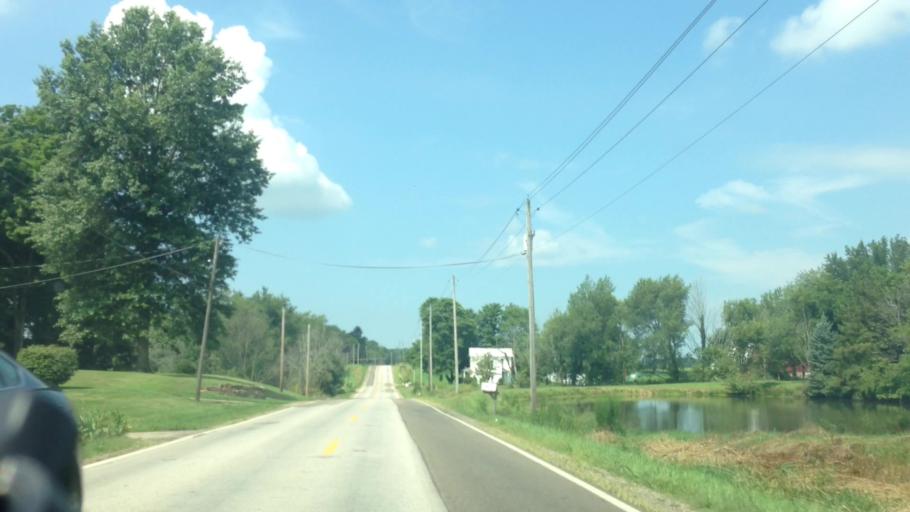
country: US
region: Ohio
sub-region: Wayne County
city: Orrville
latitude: 40.8738
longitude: -81.7421
